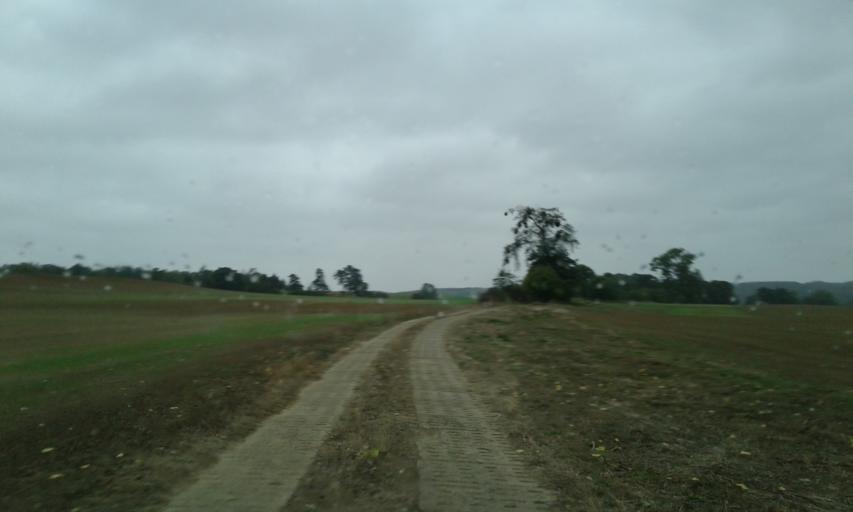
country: PL
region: West Pomeranian Voivodeship
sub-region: Powiat stargardzki
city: Dolice
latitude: 53.0974
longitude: 15.2161
